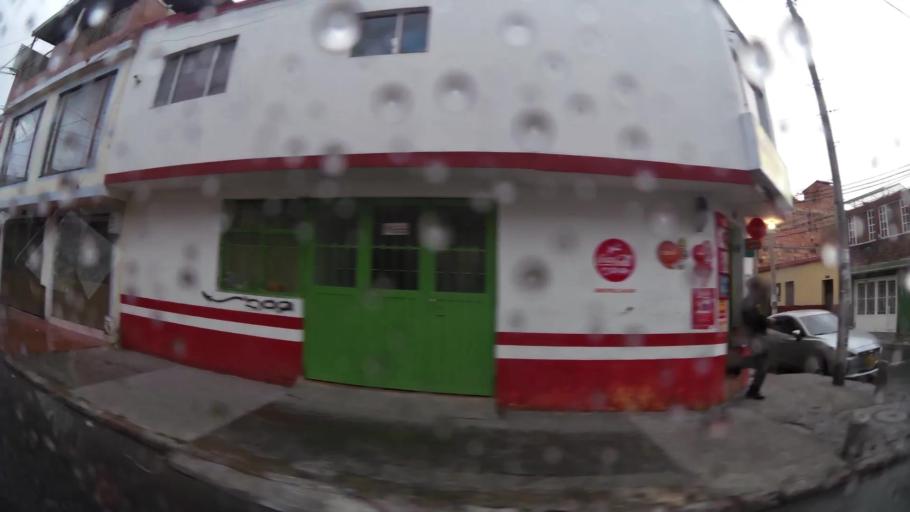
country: CO
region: Bogota D.C.
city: Bogota
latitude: 4.5897
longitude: -74.1363
